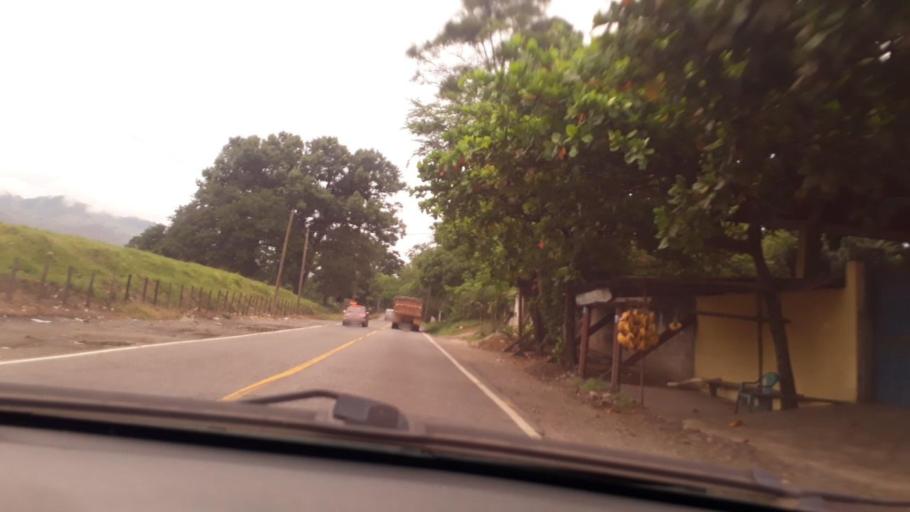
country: GT
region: Izabal
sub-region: Municipio de Los Amates
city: Los Amates
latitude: 15.2930
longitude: -89.0646
